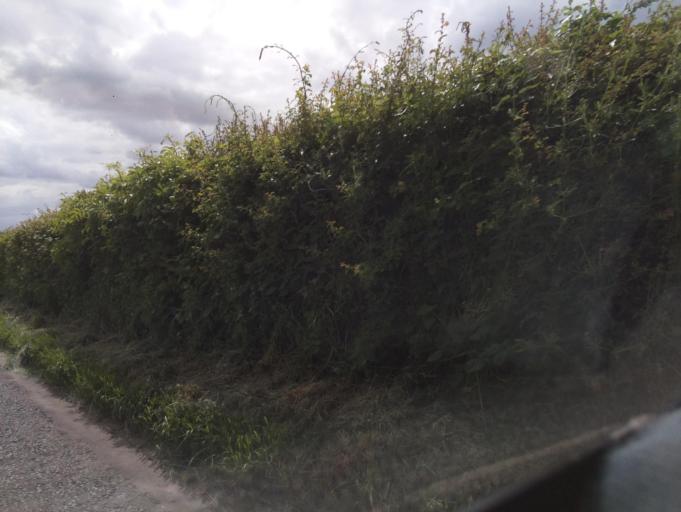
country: GB
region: England
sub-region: Herefordshire
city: Evesbatch
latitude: 52.1058
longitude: -2.4128
